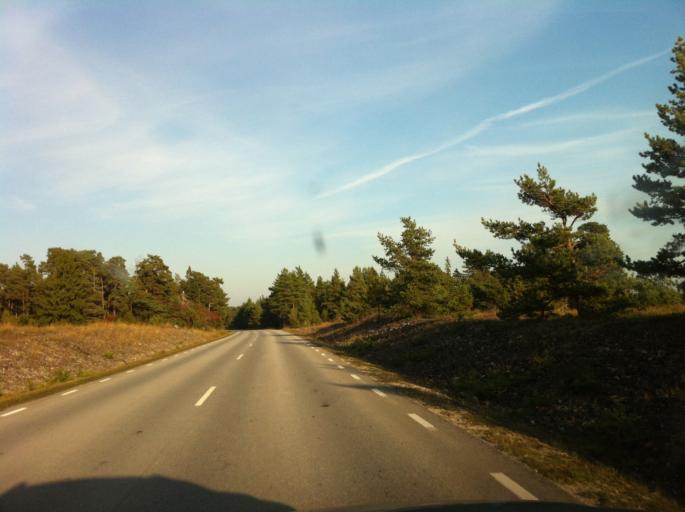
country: SE
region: Gotland
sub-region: Gotland
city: Slite
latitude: 57.4260
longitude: 18.7833
